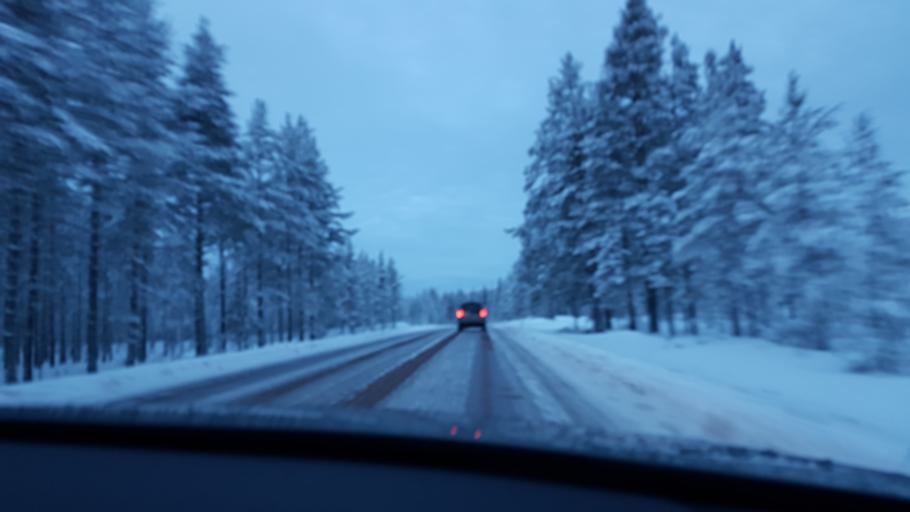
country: SE
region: Jaemtland
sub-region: Harjedalens Kommun
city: Sveg
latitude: 62.0573
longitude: 14.5920
